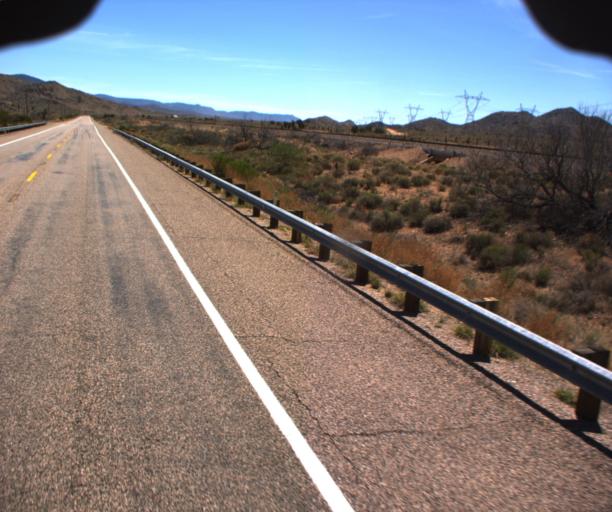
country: US
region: Arizona
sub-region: Mohave County
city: New Kingman-Butler
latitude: 35.3946
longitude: -113.7494
